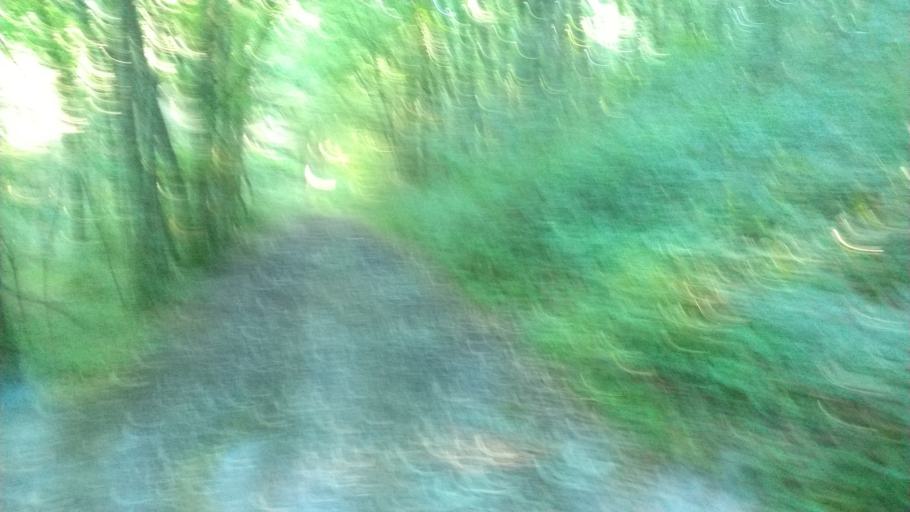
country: BE
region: Wallonia
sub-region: Province du Luxembourg
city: Tellin
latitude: 50.1122
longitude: 5.2082
